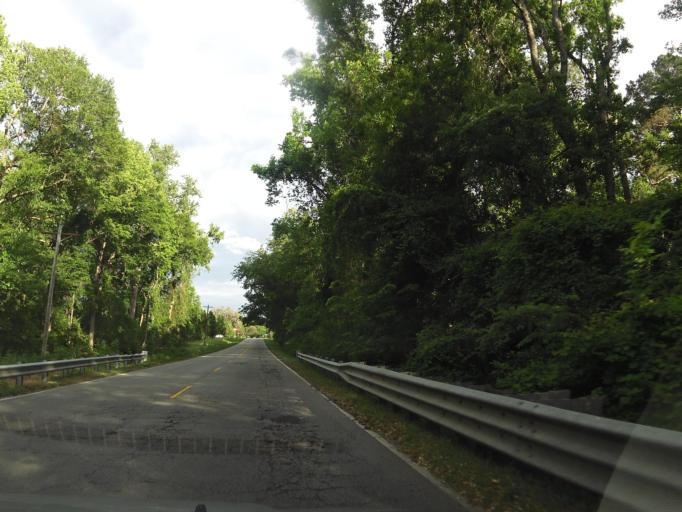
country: US
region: South Carolina
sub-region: Hampton County
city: Estill
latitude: 32.5884
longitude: -81.2016
